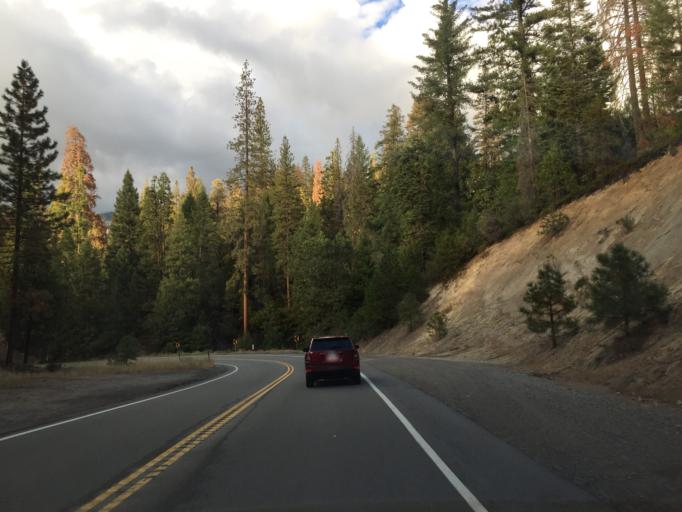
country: US
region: California
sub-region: Madera County
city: Ahwahnee
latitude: 37.5237
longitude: -119.6184
